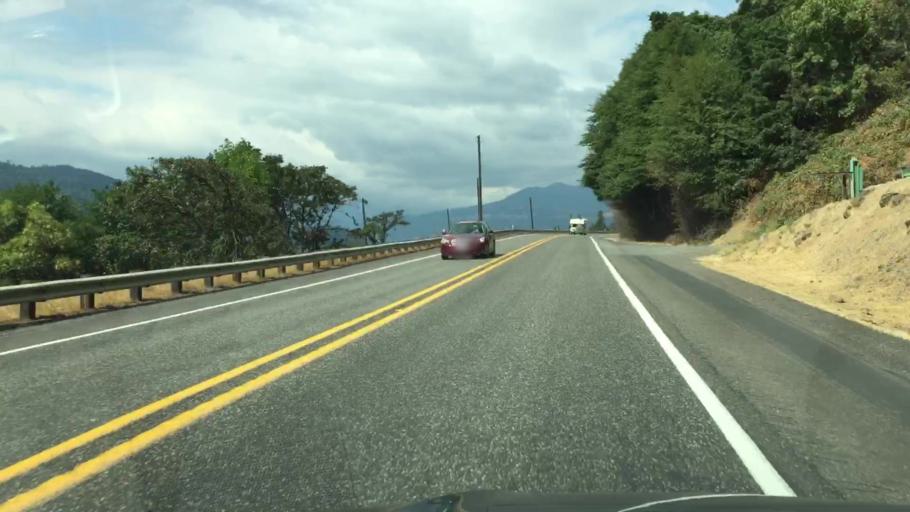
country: US
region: Washington
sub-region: Klickitat County
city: White Salmon
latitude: 45.6999
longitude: -121.4265
